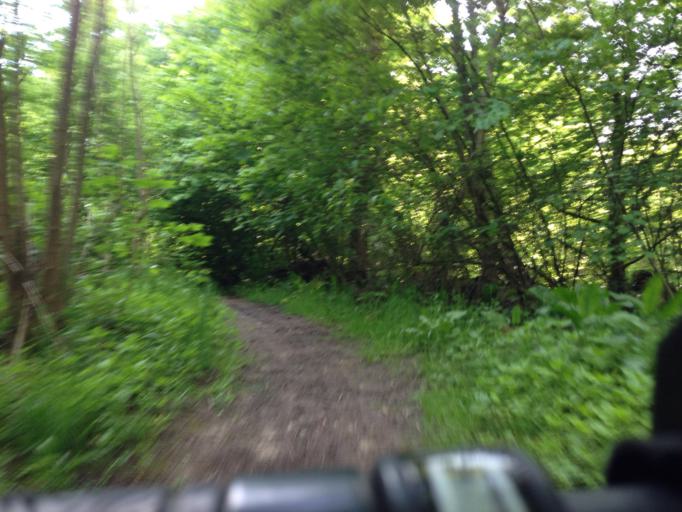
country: DE
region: Schleswig-Holstein
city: Barsbuettel
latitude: 53.5953
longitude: 10.1810
